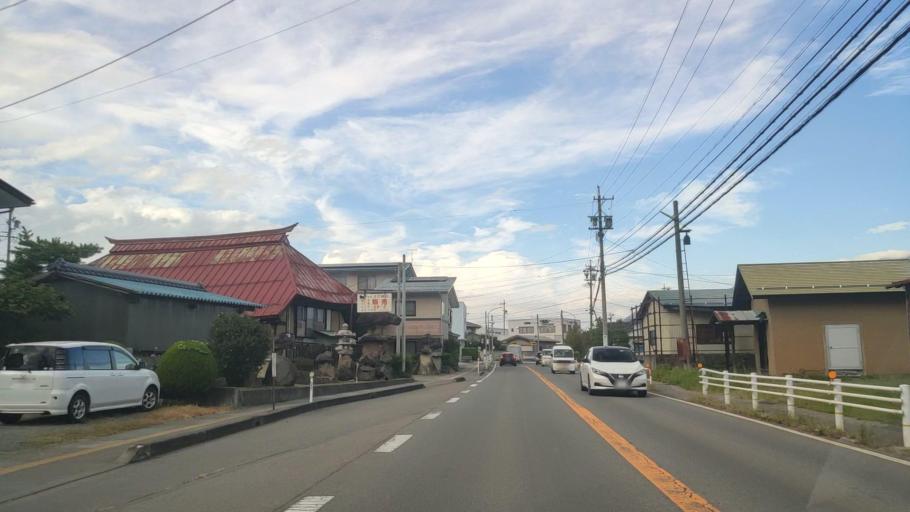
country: JP
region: Nagano
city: Nakano
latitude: 36.7397
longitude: 138.3481
